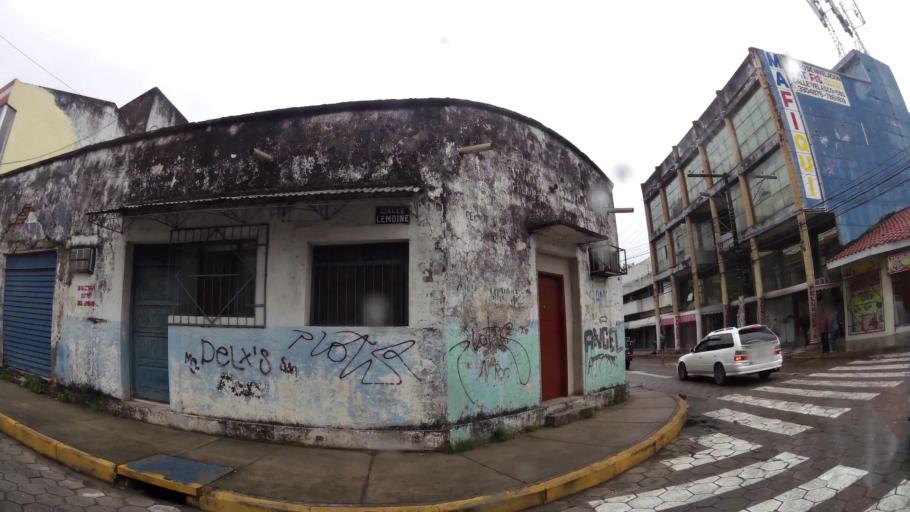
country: BO
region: Santa Cruz
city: Santa Cruz de la Sierra
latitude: -17.7903
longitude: -63.1830
